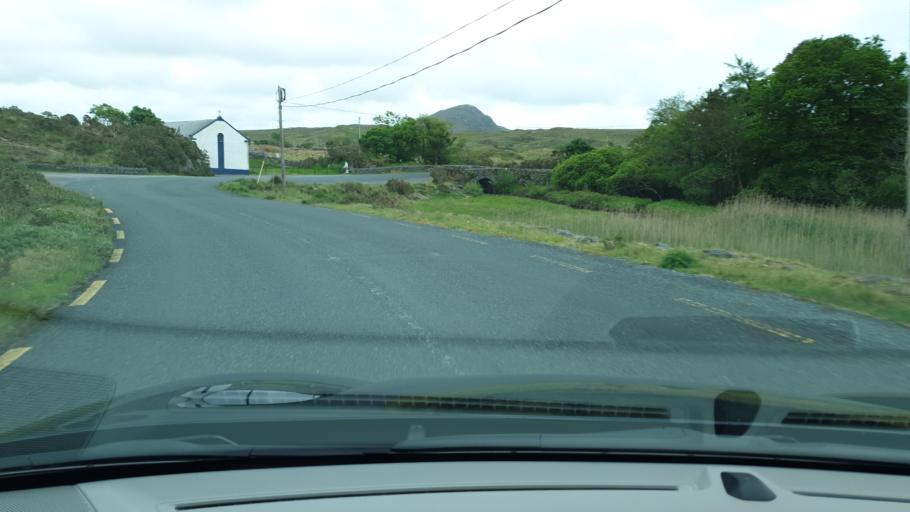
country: IE
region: Connaught
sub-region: County Galway
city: Clifden
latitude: 53.4596
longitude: -9.8107
